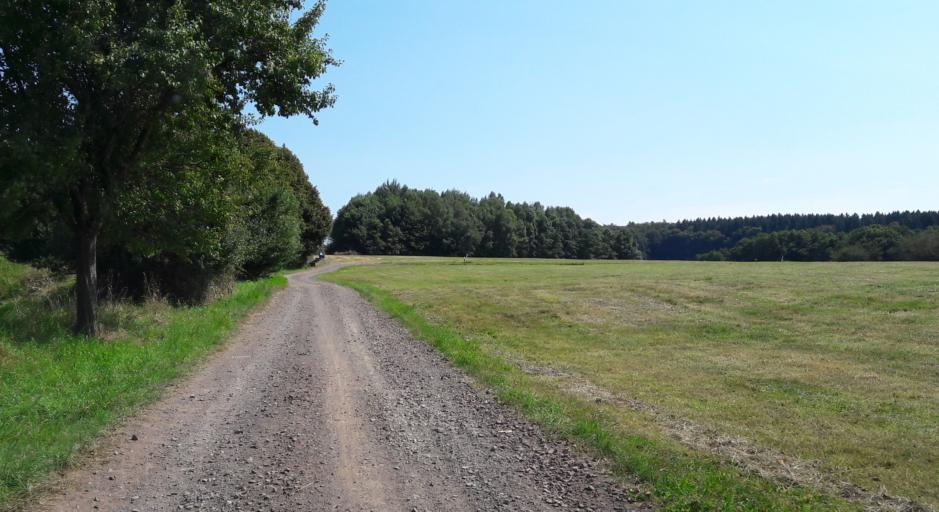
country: DE
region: Saarland
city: Mainzweiler
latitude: 49.4077
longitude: 7.1132
